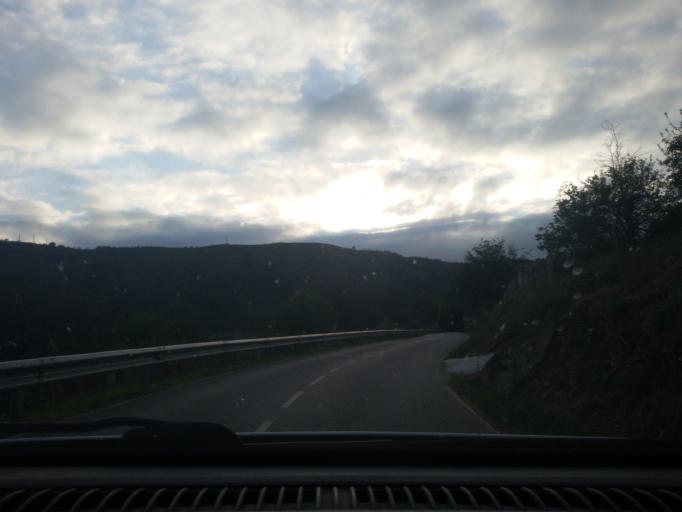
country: ES
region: Asturias
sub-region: Province of Asturias
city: Bimenes
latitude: 43.3340
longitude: -5.5847
